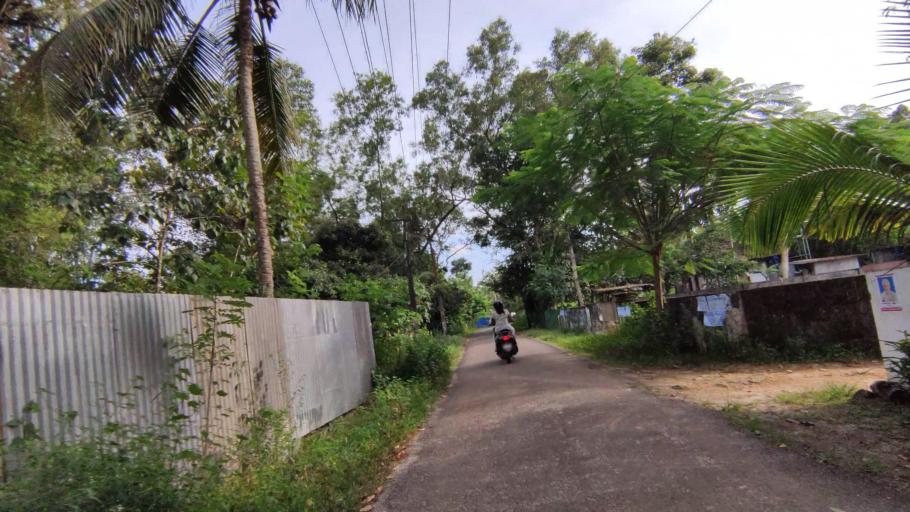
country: IN
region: Kerala
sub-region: Alappuzha
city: Shertallai
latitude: 9.6415
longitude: 76.3394
